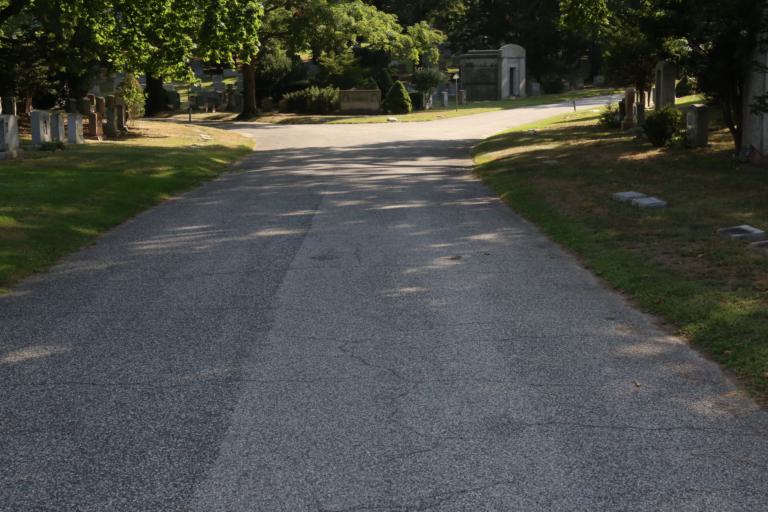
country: US
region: New York
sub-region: Bronx
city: The Bronx
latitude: 40.8837
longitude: -73.8723
